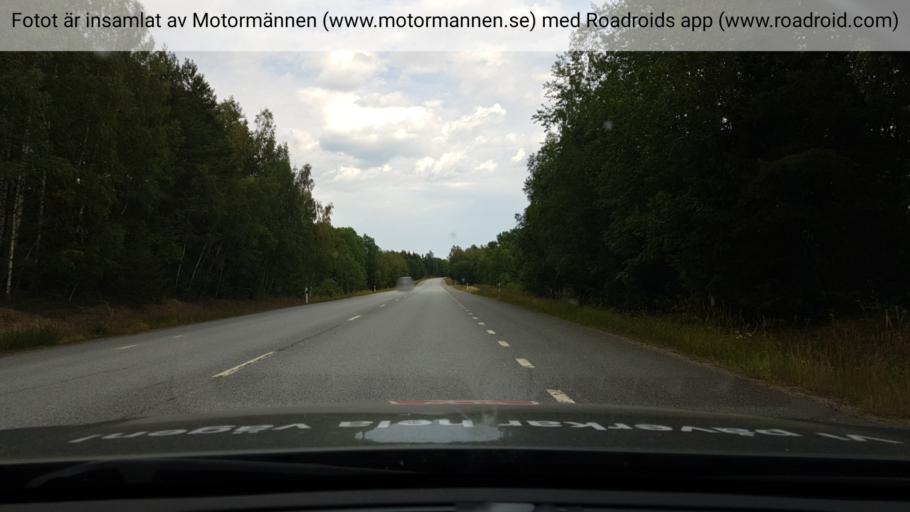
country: SE
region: Uppsala
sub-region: Heby Kommun
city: Morgongava
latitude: 59.8940
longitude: 17.1430
